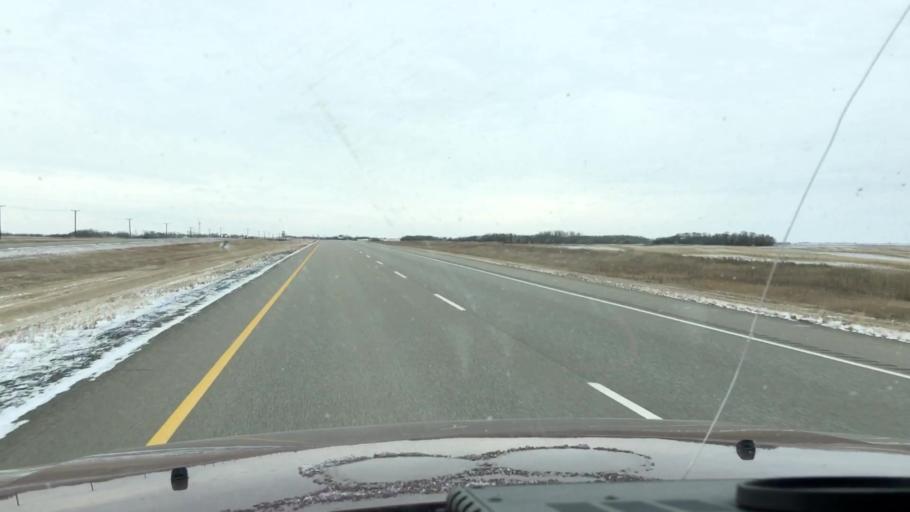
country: CA
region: Saskatchewan
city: Watrous
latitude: 51.3935
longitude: -106.1705
